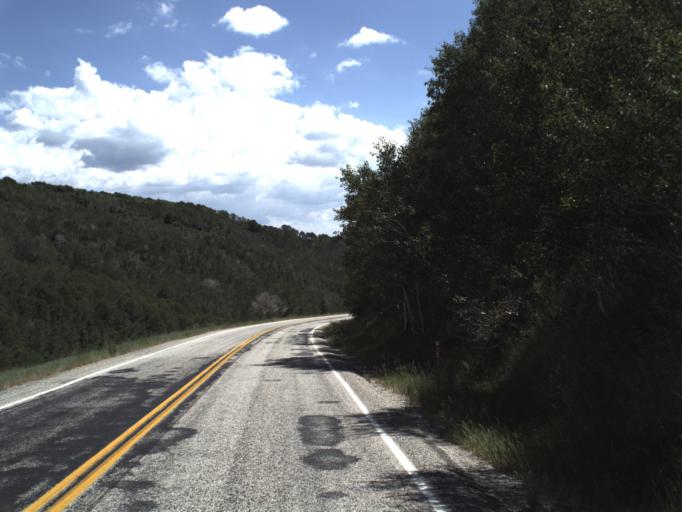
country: US
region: Utah
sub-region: Weber County
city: Wolf Creek
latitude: 41.4180
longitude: -111.5760
